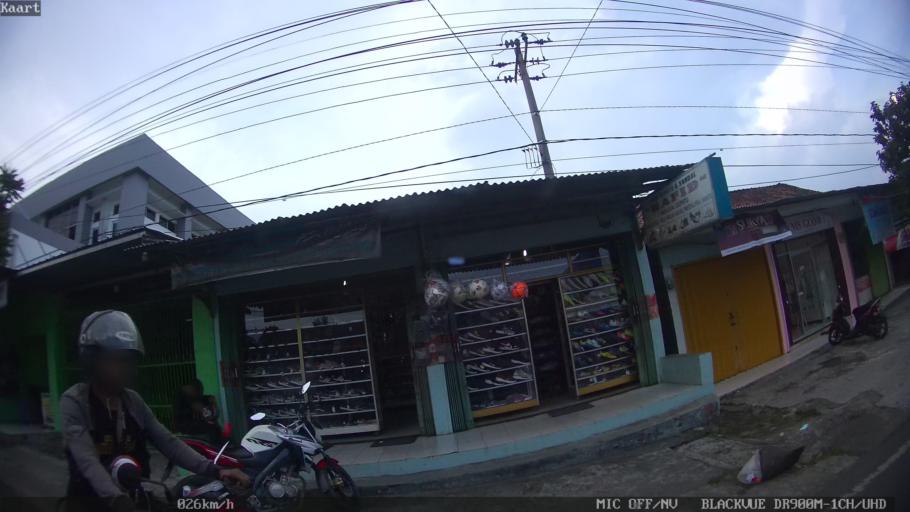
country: ID
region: Lampung
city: Kedaton
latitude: -5.3927
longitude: 105.2168
